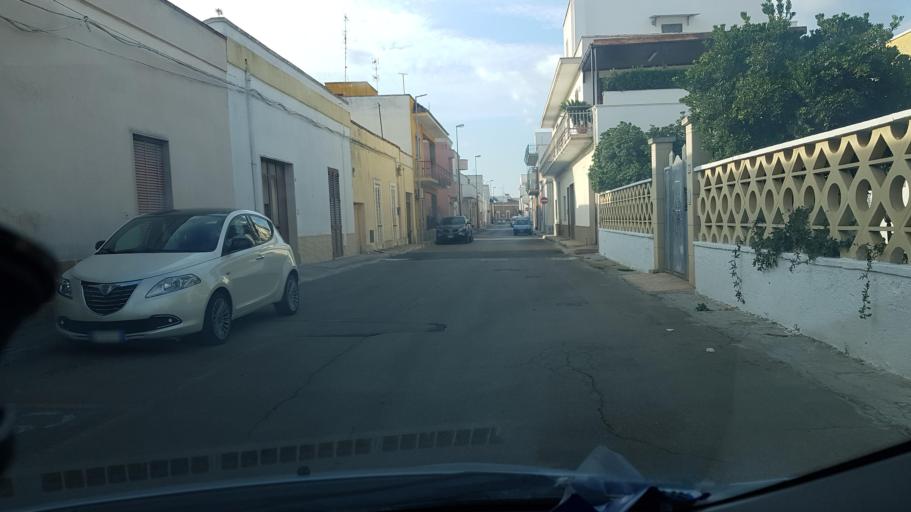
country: IT
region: Apulia
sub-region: Provincia di Lecce
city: Veglie
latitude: 40.3287
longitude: 17.9698
